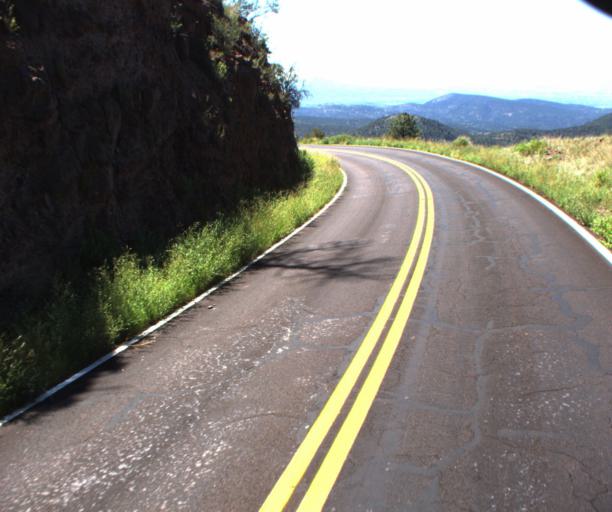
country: US
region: Arizona
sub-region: Greenlee County
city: Morenci
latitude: 33.4335
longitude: -109.3769
